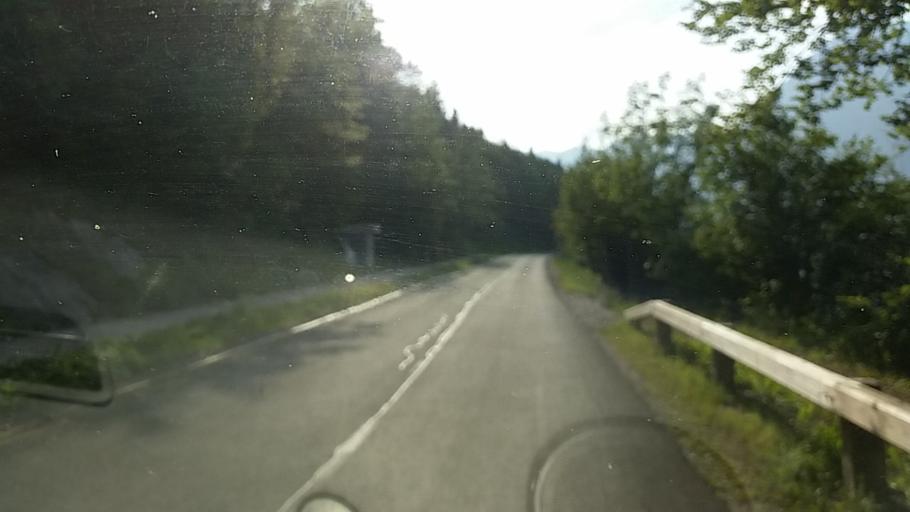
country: SI
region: Bohinj
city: Bohinjska Bistrica
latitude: 46.2777
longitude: 13.8792
